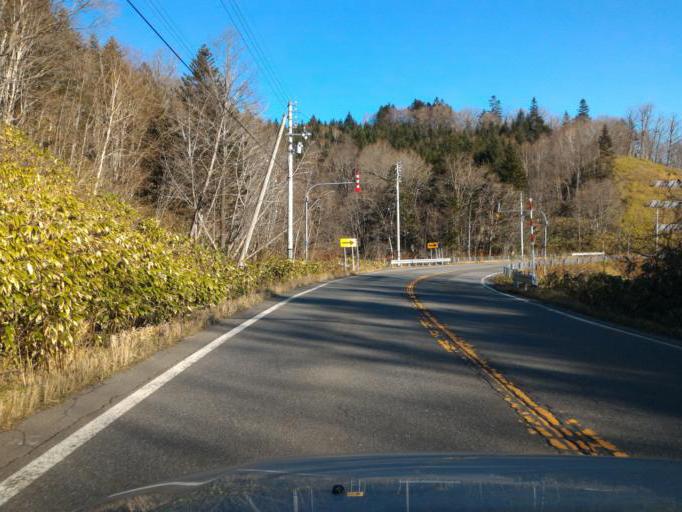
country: JP
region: Hokkaido
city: Bibai
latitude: 43.2786
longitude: 142.0557
